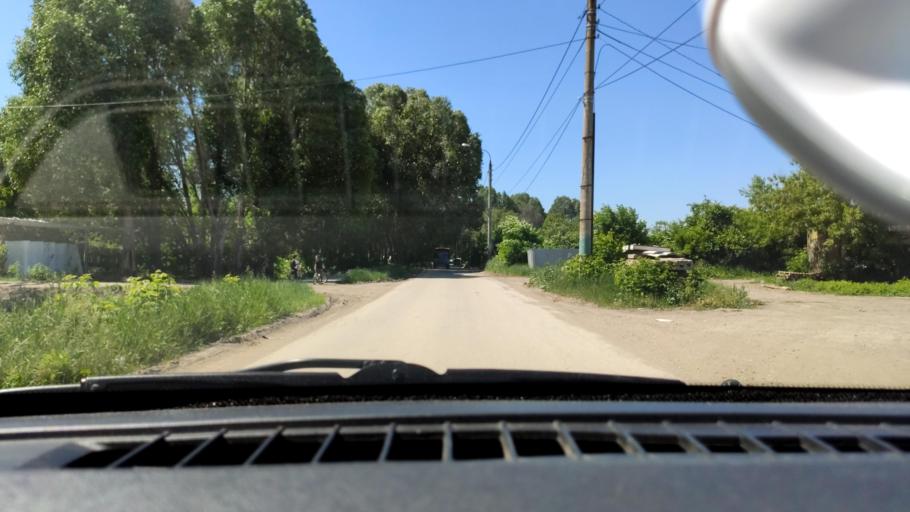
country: RU
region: Samara
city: Smyshlyayevka
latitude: 53.1891
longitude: 50.2841
